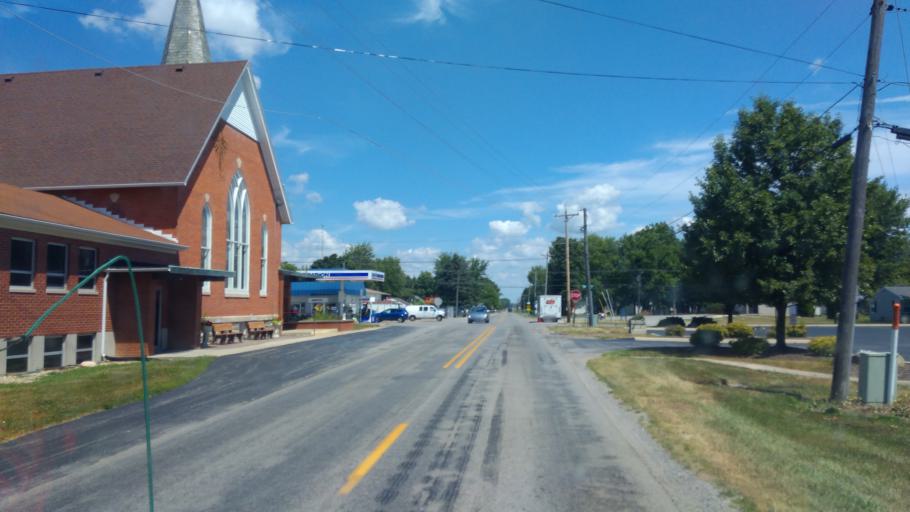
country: US
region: Indiana
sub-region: Allen County
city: New Haven
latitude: 40.9474
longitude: -84.9979
